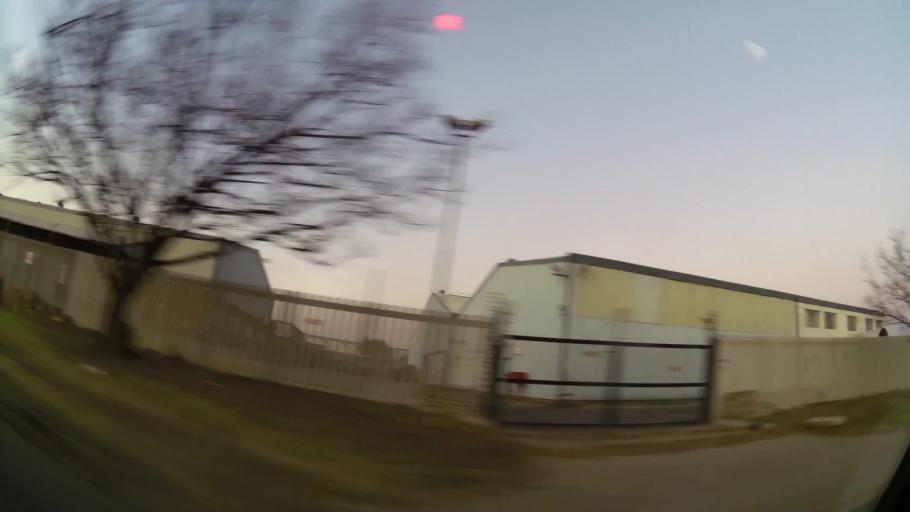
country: ZA
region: Gauteng
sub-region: Ekurhuleni Metropolitan Municipality
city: Germiston
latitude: -26.2719
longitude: 28.1741
